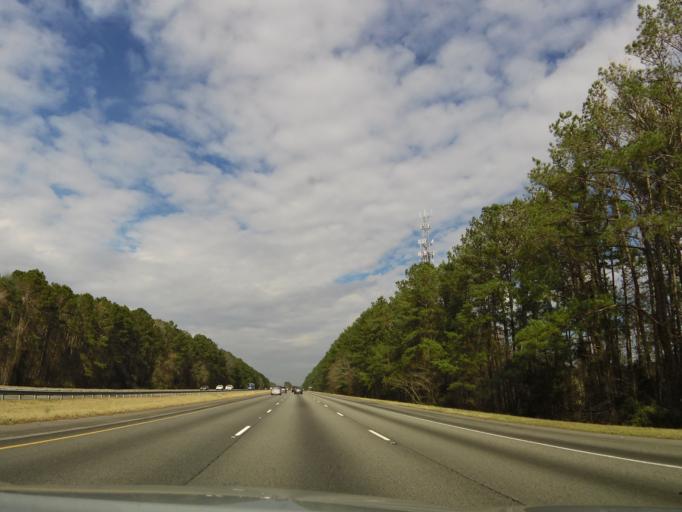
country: US
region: Georgia
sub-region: Bryan County
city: Richmond Hill
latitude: 31.8516
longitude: -81.3429
